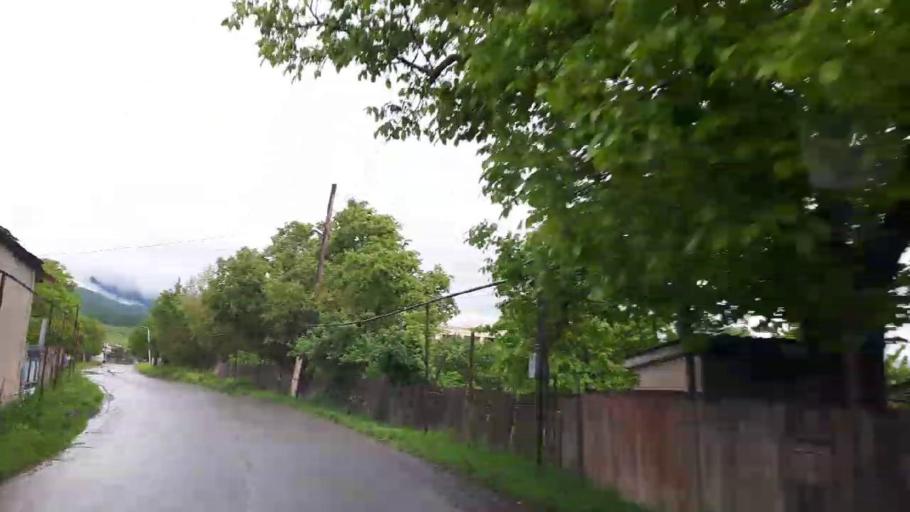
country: GE
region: Shida Kartli
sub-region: Khashuris Raioni
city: Khashuri
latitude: 41.9832
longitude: 43.6657
